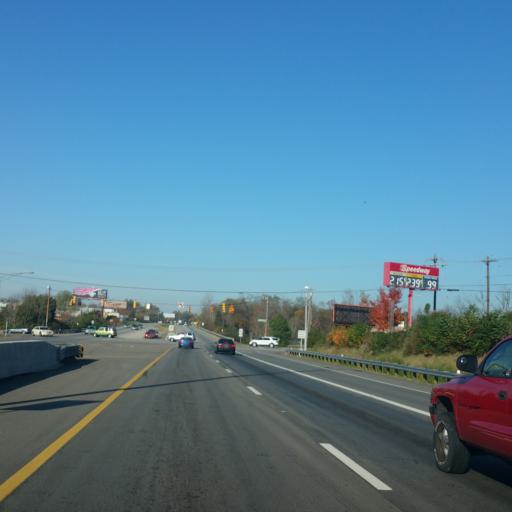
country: US
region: Ohio
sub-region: Clermont County
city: Summerside
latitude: 39.1038
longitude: -84.2906
